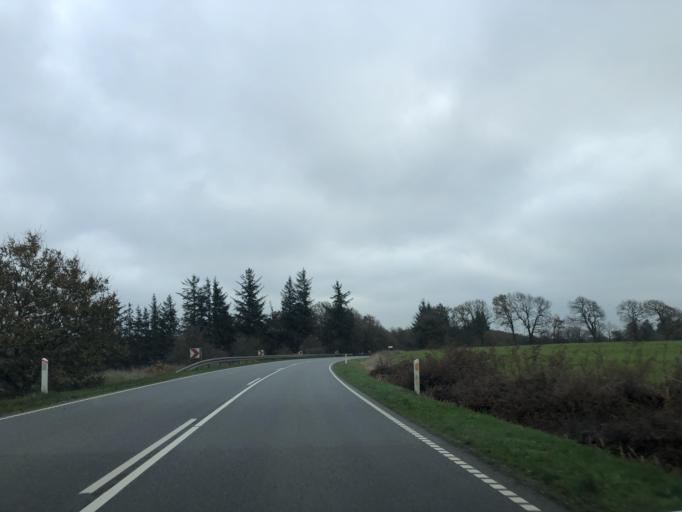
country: DK
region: South Denmark
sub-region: Haderslev Kommune
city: Gram
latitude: 55.2508
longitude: 8.9208
